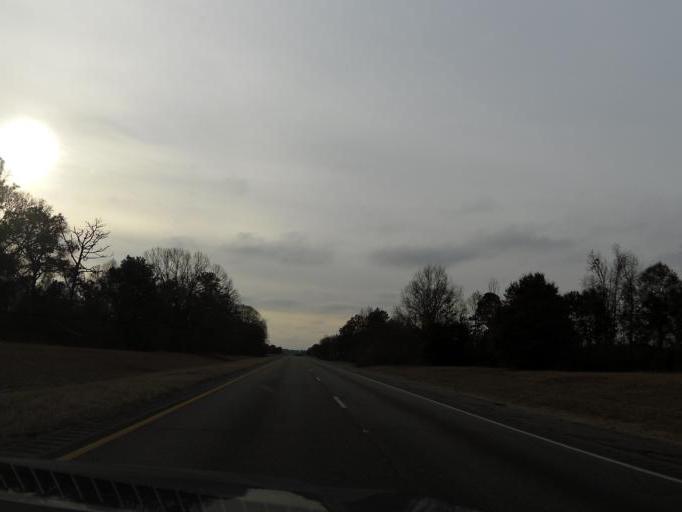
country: US
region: Alabama
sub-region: Autauga County
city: Pine Level
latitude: 32.5727
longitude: -86.4673
